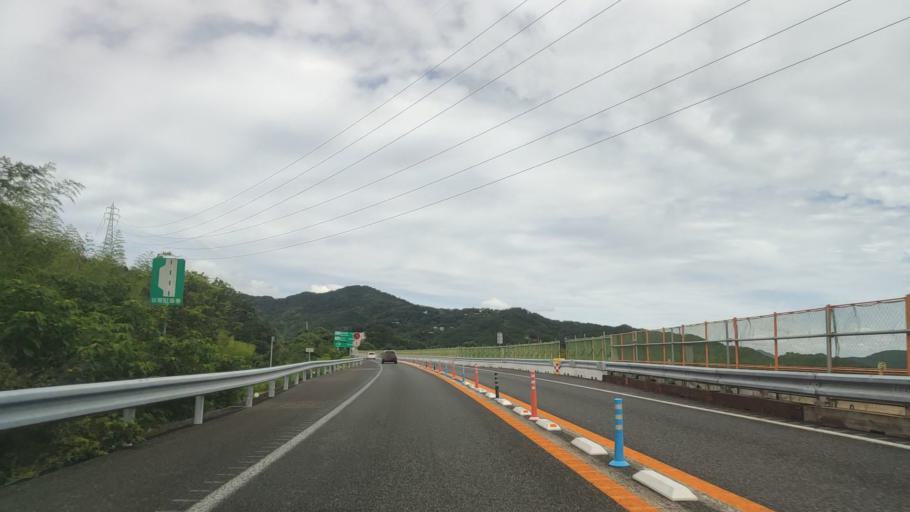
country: JP
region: Wakayama
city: Gobo
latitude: 33.8383
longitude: 135.2206
